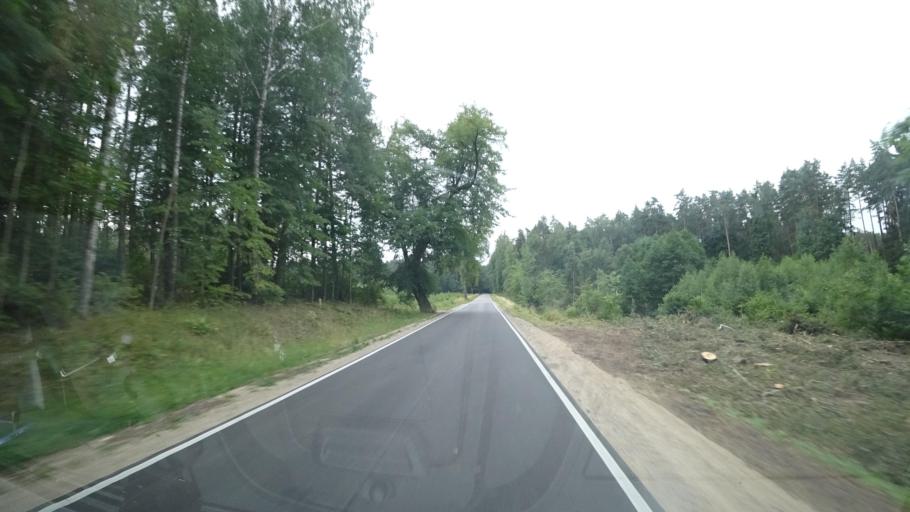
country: PL
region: Warmian-Masurian Voivodeship
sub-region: Powiat gizycki
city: Ryn
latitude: 53.8862
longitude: 21.5762
